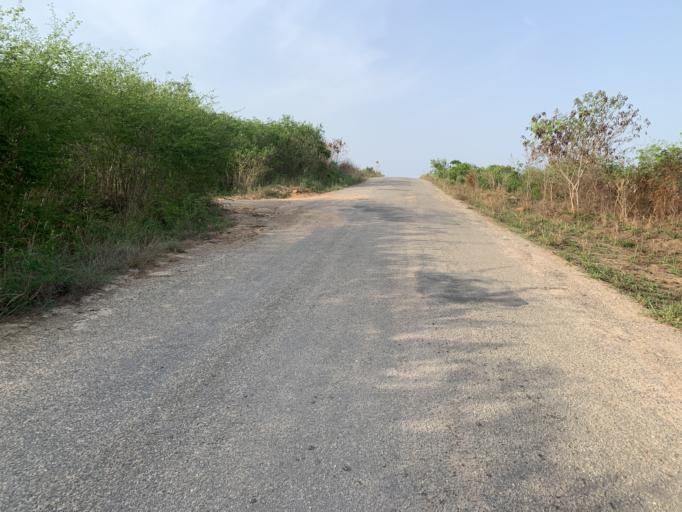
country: GH
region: Central
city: Winneba
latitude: 5.3856
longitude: -0.6055
